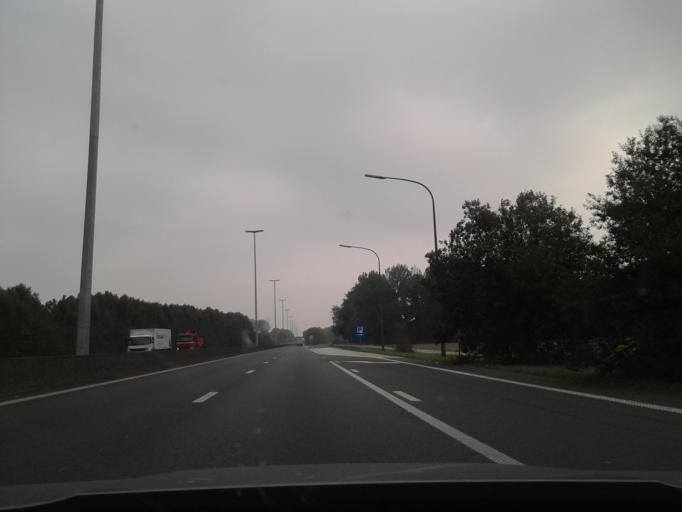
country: BE
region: Wallonia
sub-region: Province du Hainaut
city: Tournai
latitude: 50.6439
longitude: 3.4413
